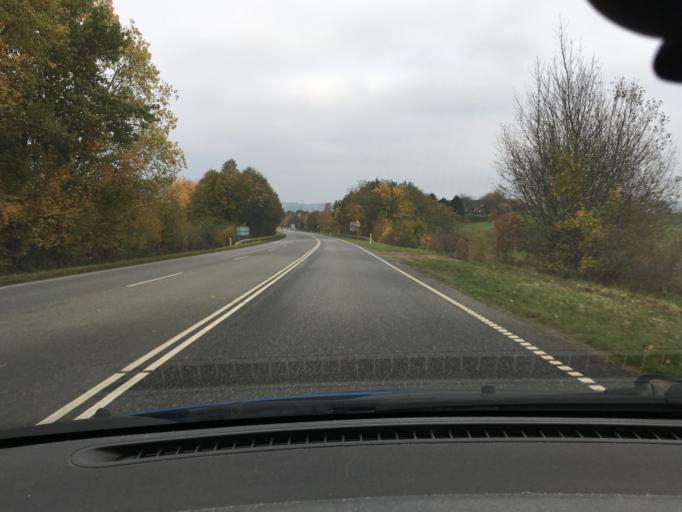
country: DK
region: South Denmark
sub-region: Aabenraa Kommune
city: Aabenraa
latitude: 55.0185
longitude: 9.4263
